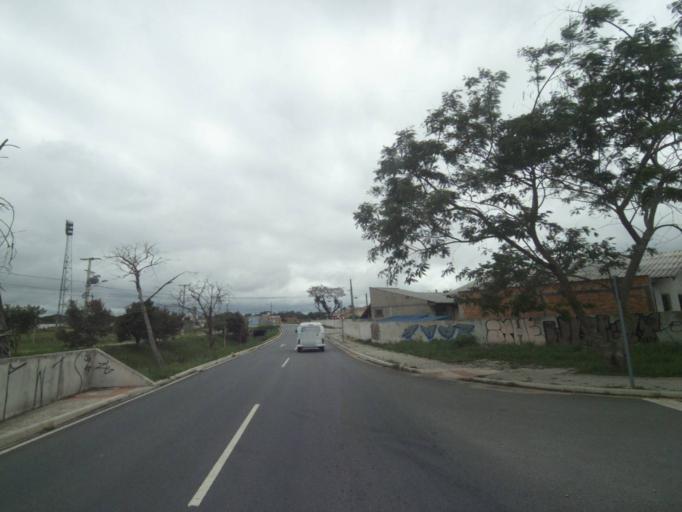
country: BR
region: Parana
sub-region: Pinhais
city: Pinhais
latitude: -25.4336
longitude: -49.2194
